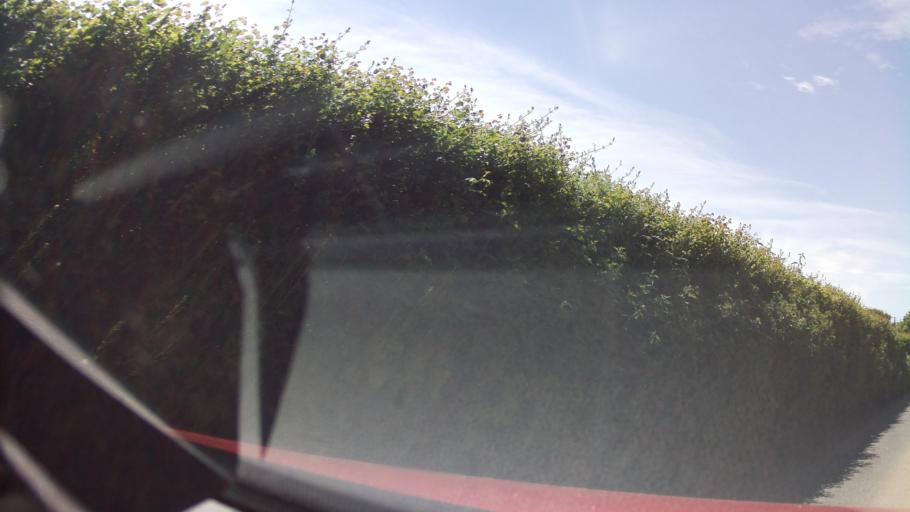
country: GB
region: England
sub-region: Devon
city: Ottery St Mary
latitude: 50.7608
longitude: -3.2716
